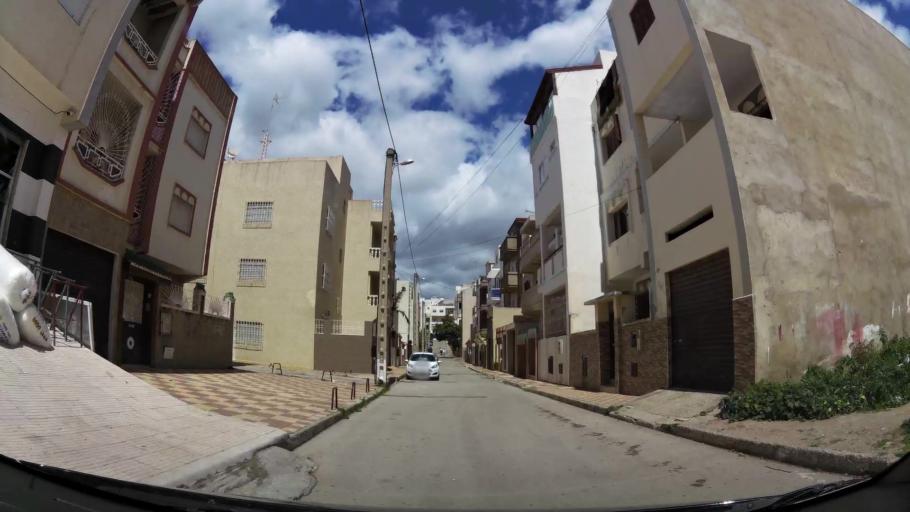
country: MA
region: Tanger-Tetouan
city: Tetouan
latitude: 35.5783
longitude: -5.3434
